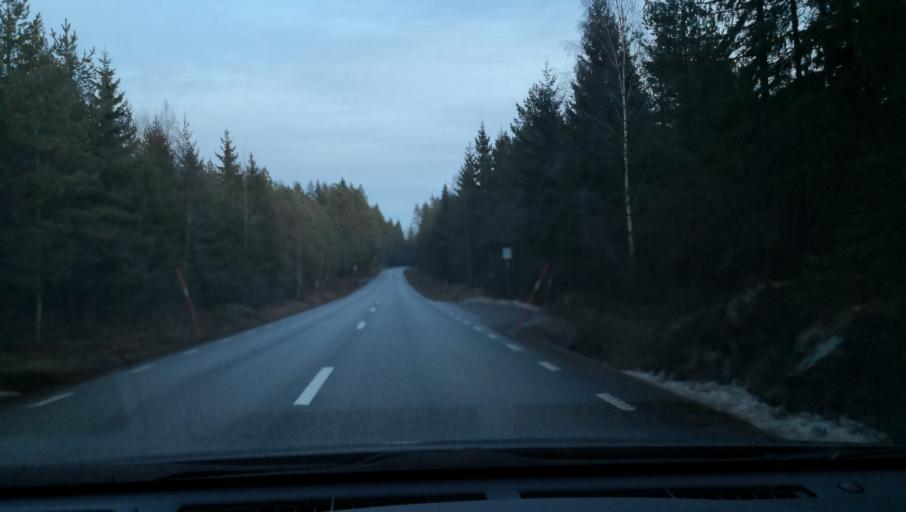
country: SE
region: OErebro
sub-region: Laxa Kommun
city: Laxa
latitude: 59.1282
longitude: 14.6093
